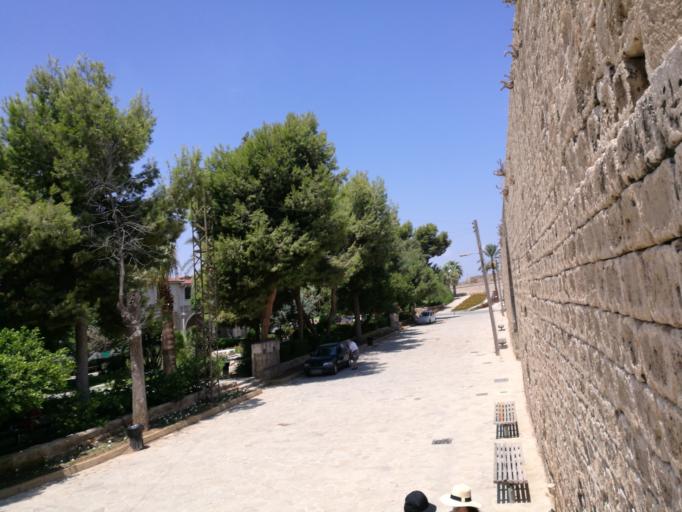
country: CY
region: Ammochostos
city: Famagusta
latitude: 35.1261
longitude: 33.9444
